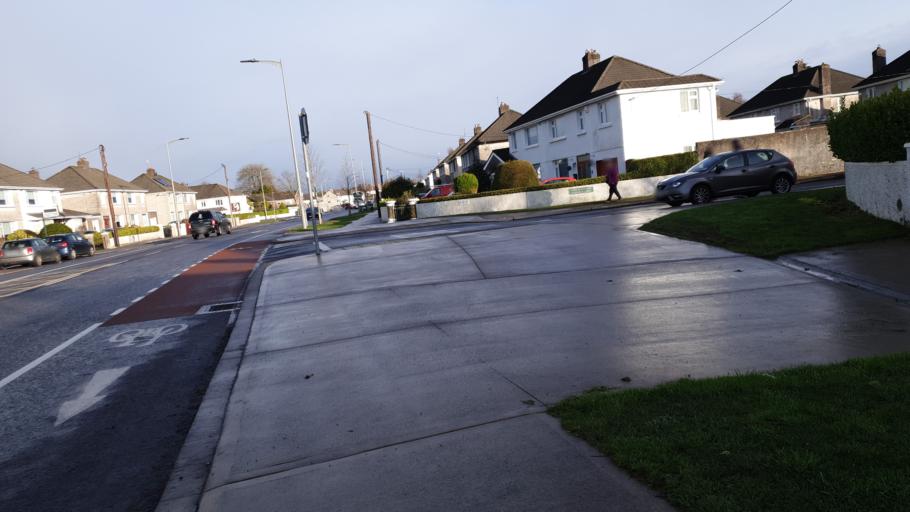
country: IE
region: Munster
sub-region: County Cork
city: Cork
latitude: 51.8877
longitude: -8.4222
